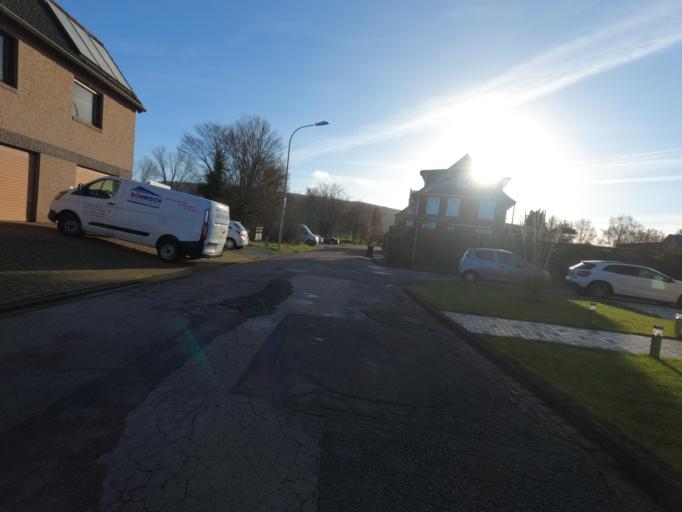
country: DE
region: North Rhine-Westphalia
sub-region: Regierungsbezirk Koln
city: Titz
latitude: 50.9474
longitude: 6.4175
